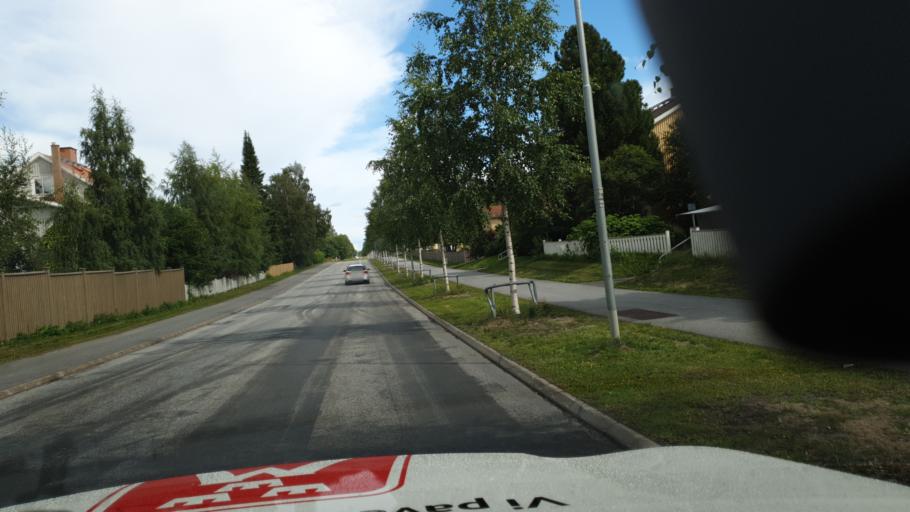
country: SE
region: Vaesterbotten
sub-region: Umea Kommun
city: Roback
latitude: 63.8362
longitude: 20.1894
